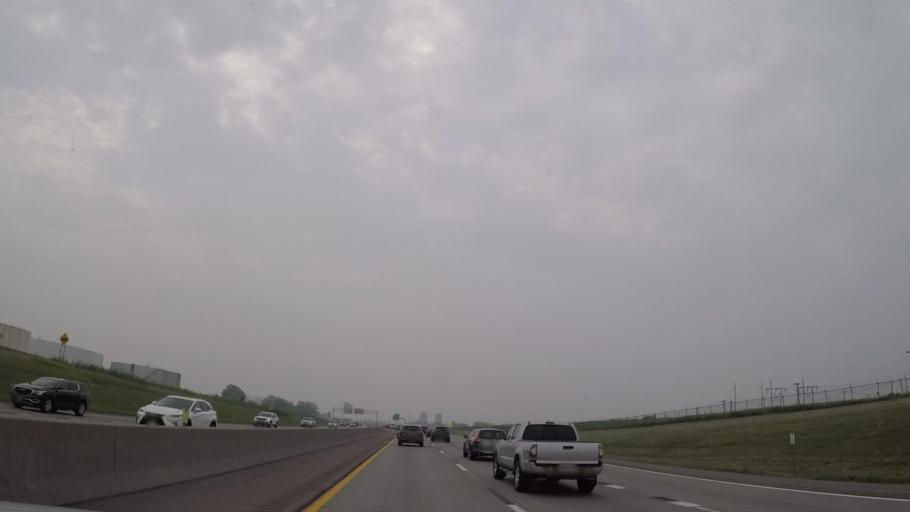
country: US
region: New York
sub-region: Erie County
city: Grandyle Village
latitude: 42.9912
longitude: -78.9225
